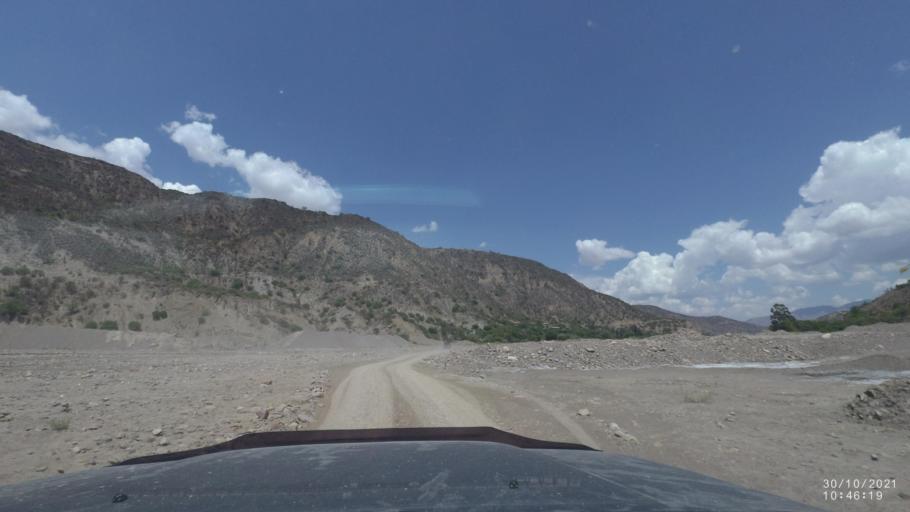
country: BO
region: Cochabamba
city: Sipe Sipe
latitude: -17.5612
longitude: -66.4562
